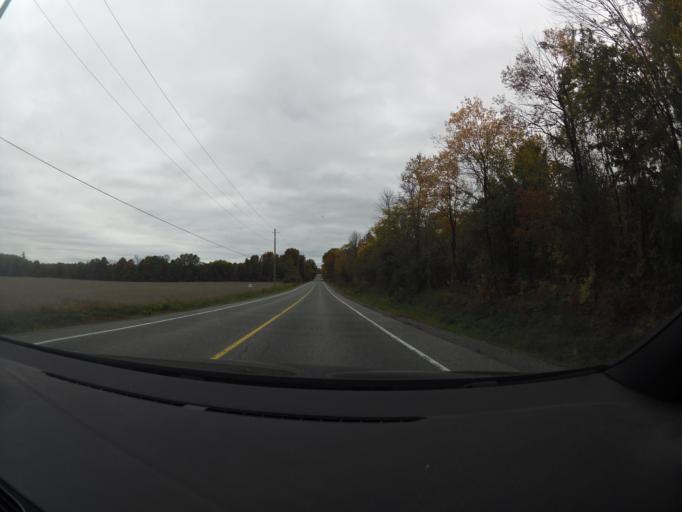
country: CA
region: Ontario
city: Bells Corners
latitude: 45.3370
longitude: -75.9803
